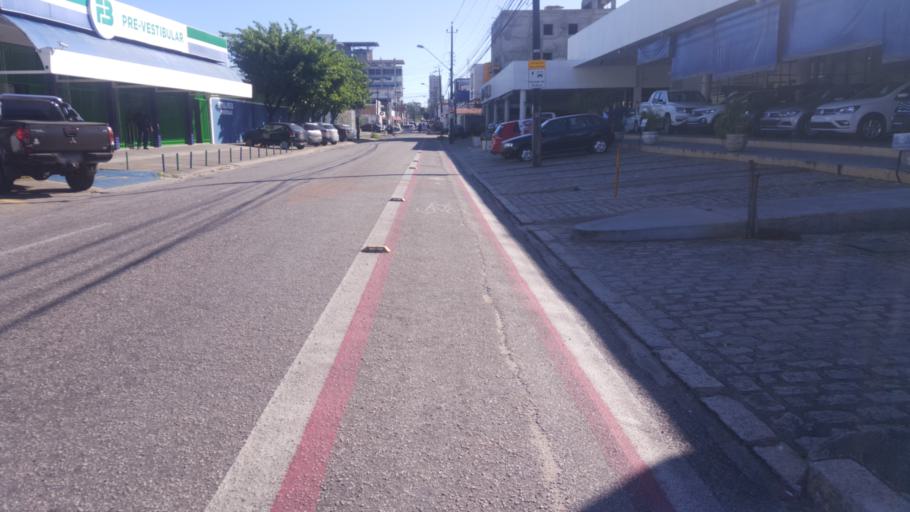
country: BR
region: Ceara
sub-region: Fortaleza
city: Fortaleza
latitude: -3.7396
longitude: -38.5324
